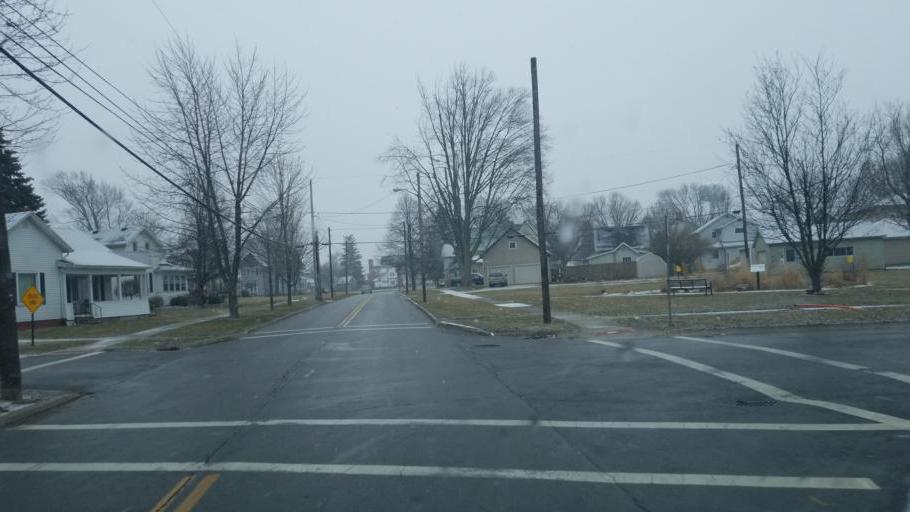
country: US
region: Ohio
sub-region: Defiance County
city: Hicksville
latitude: 41.2956
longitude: -84.7662
